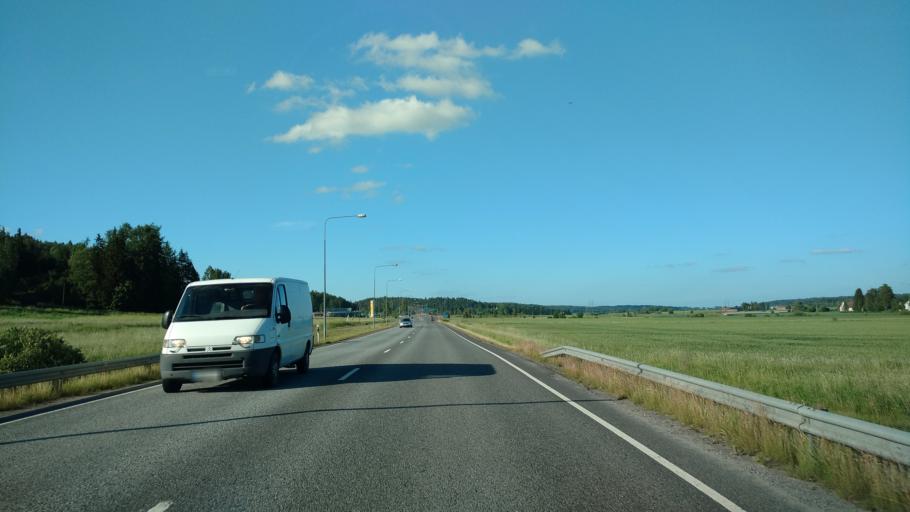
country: FI
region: Varsinais-Suomi
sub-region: Salo
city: Salo
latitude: 60.4113
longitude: 23.1589
